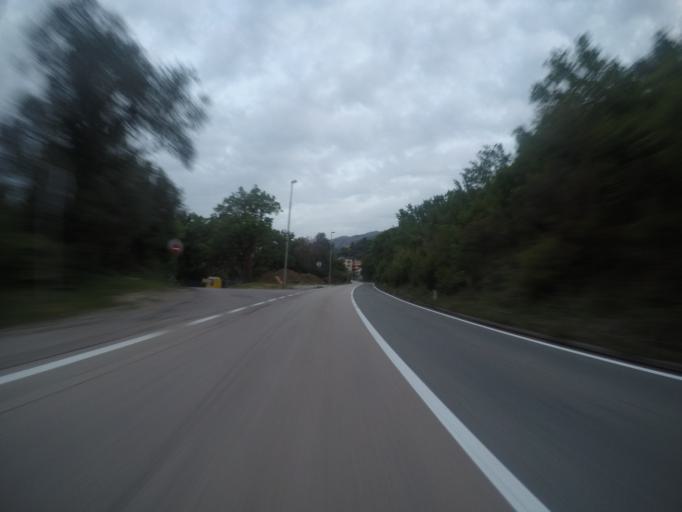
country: ME
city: Petrovac na Moru
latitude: 42.1980
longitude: 18.9690
